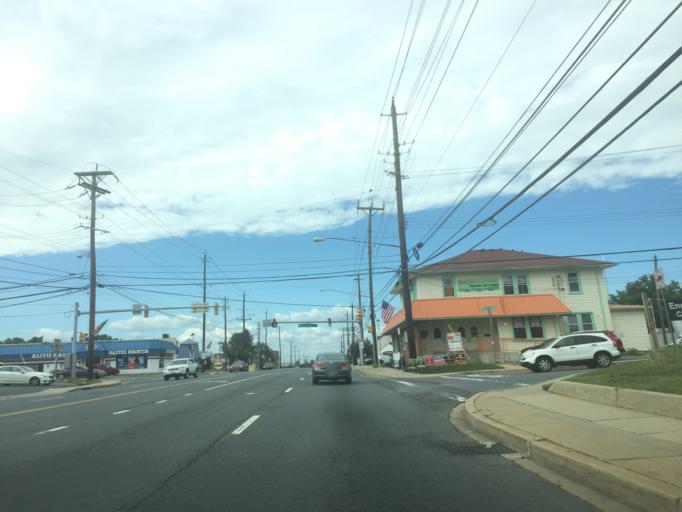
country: US
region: Maryland
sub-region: Montgomery County
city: Gaithersburg
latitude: 39.1436
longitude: -77.2010
